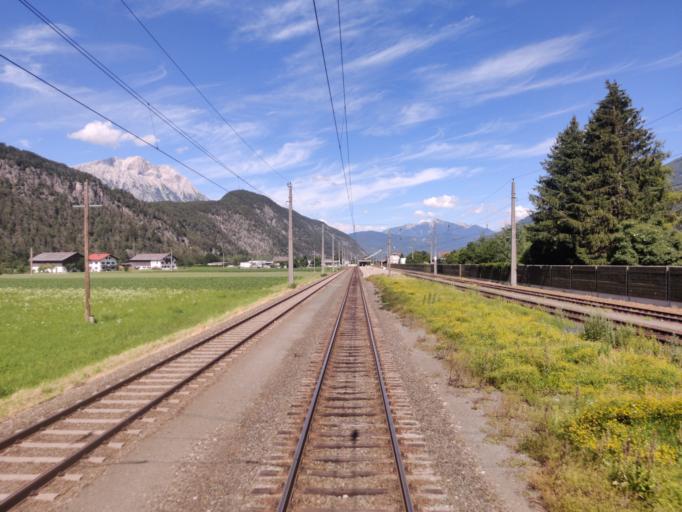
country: AT
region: Tyrol
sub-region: Politischer Bezirk Imst
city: Stams
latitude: 47.2807
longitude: 10.9751
